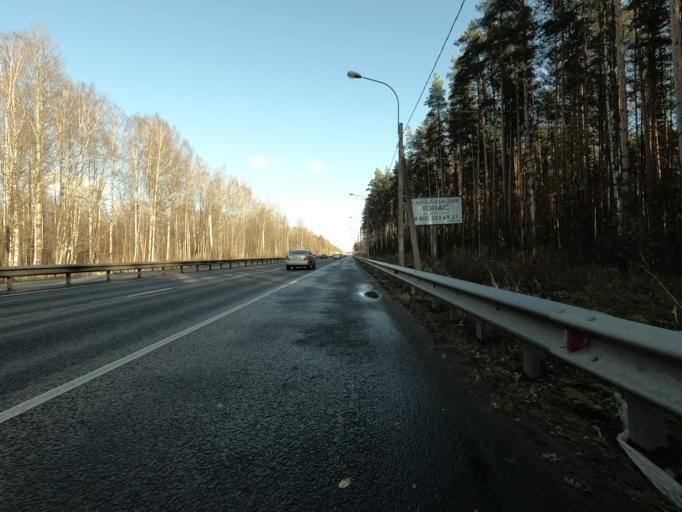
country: RU
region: St.-Petersburg
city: Krasnogvargeisky
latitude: 59.9985
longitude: 30.5496
